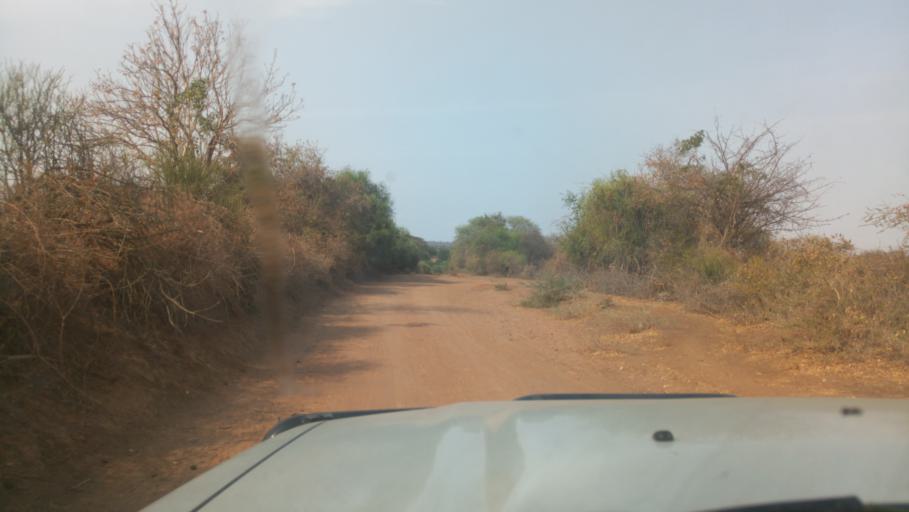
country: KE
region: Kitui
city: Kitui
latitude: -1.5989
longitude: 37.8798
